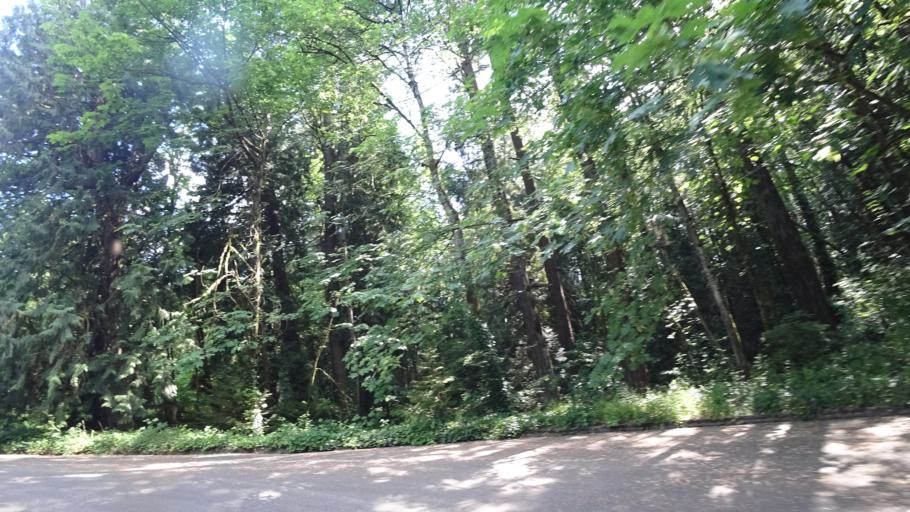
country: US
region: Oregon
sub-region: Washington County
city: Garden Home-Whitford
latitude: 45.4718
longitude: -122.7179
